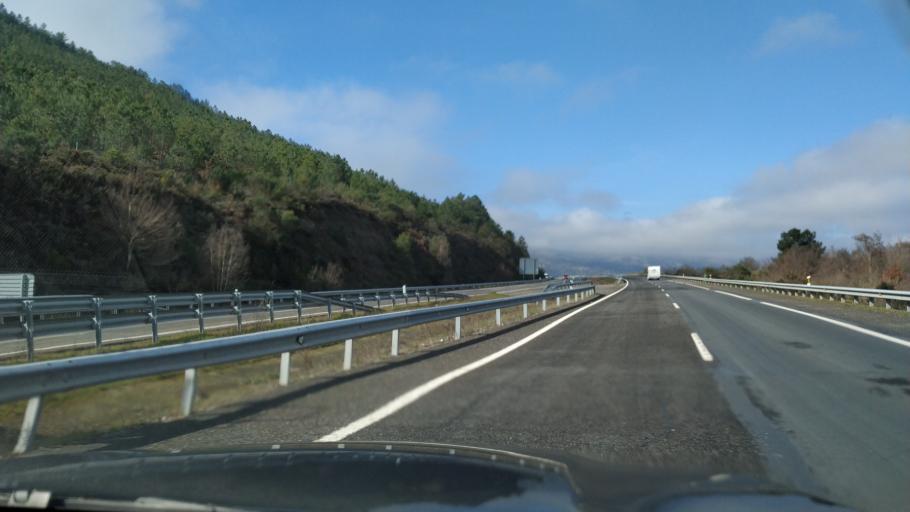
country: ES
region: Galicia
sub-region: Provincia de Ourense
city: Verin
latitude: 41.9202
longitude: -7.4570
